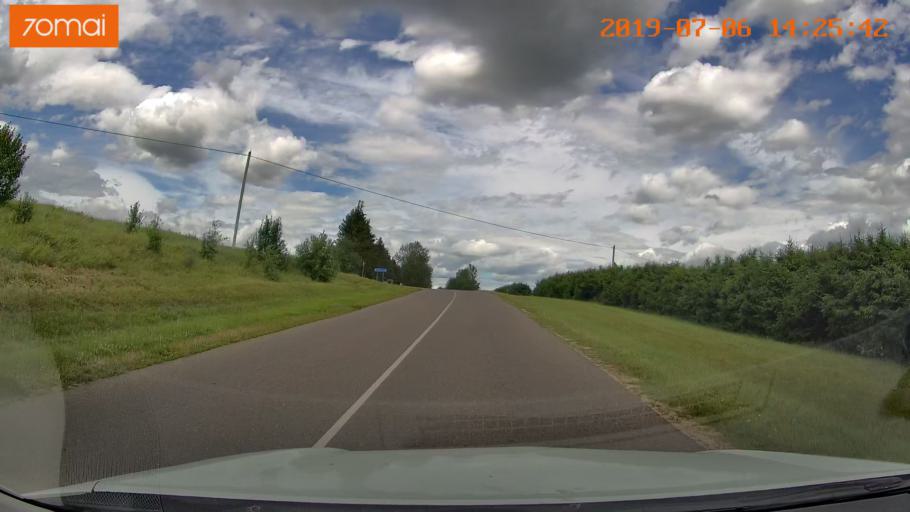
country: BY
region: Minsk
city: Ivyanyets
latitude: 53.9319
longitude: 26.7947
